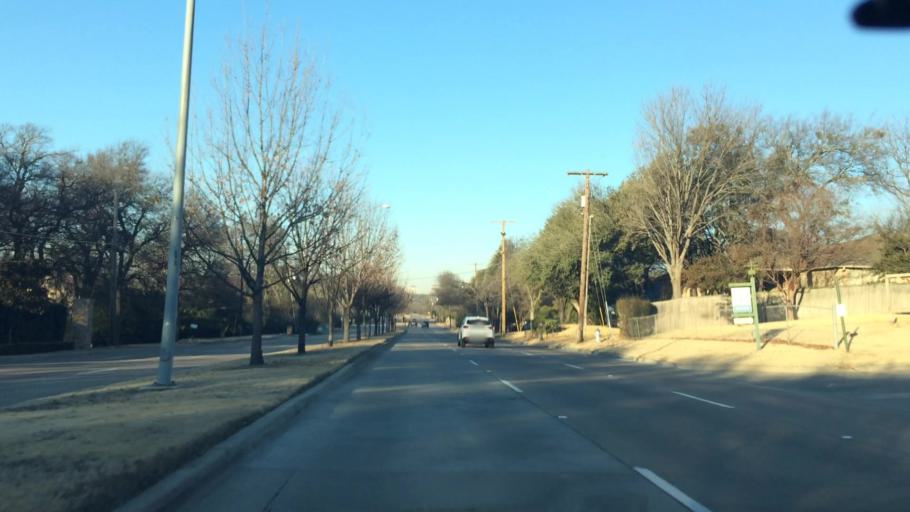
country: US
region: Texas
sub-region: Dallas County
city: Addison
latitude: 32.9400
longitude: -96.7881
